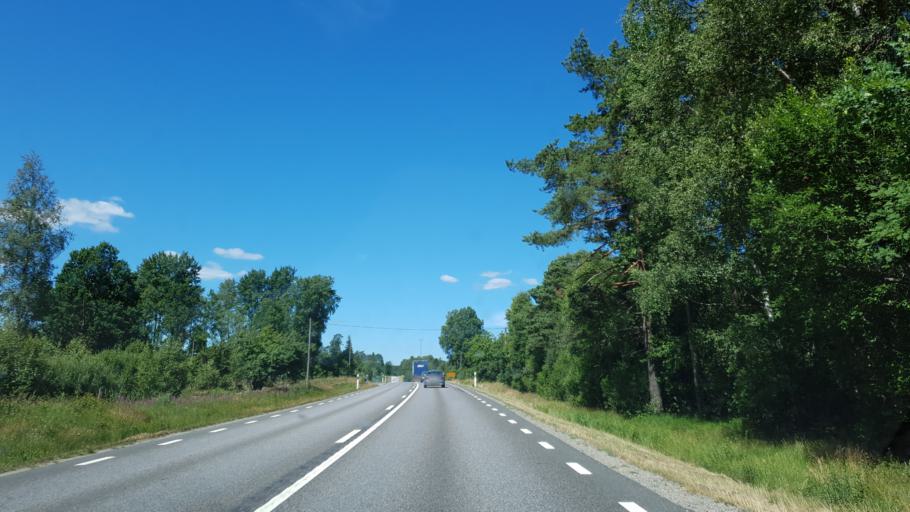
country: SE
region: Joenkoeping
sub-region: Varnamo Kommun
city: Rydaholm
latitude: 56.9365
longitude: 14.3861
